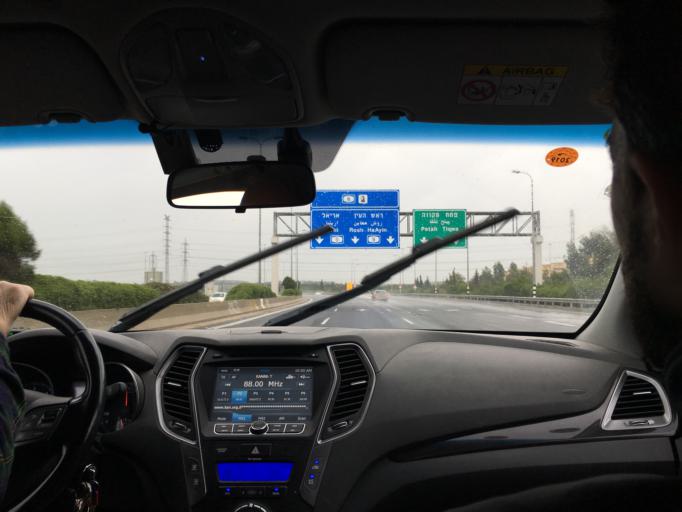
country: IL
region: Central District
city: Petah Tiqwa
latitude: 32.1185
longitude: 34.8732
